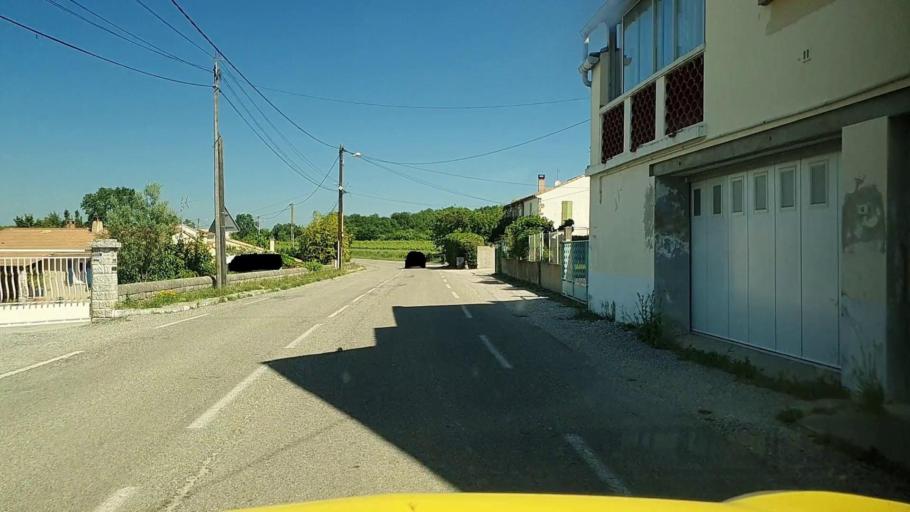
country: FR
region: Languedoc-Roussillon
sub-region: Departement du Gard
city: Moussac
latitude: 43.9833
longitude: 4.2307
